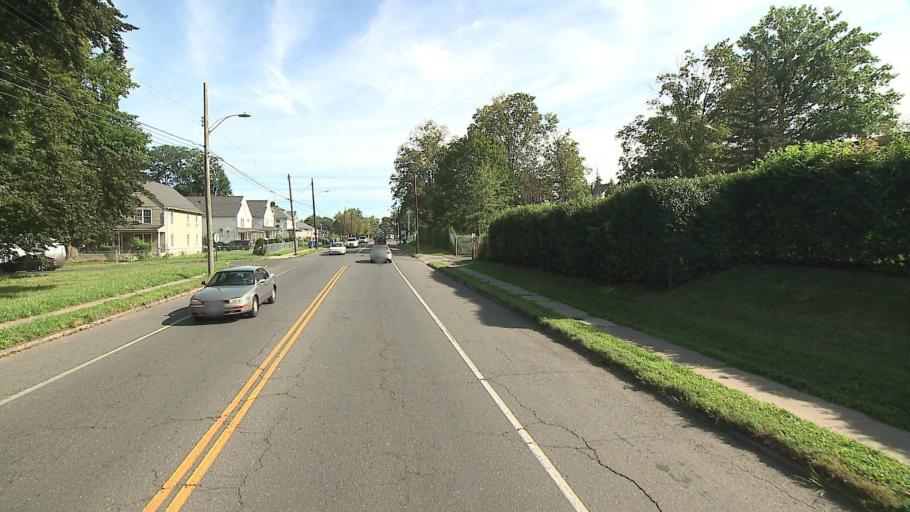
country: US
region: Connecticut
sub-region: Hartford County
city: Blue Hills
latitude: 41.7973
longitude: -72.6961
